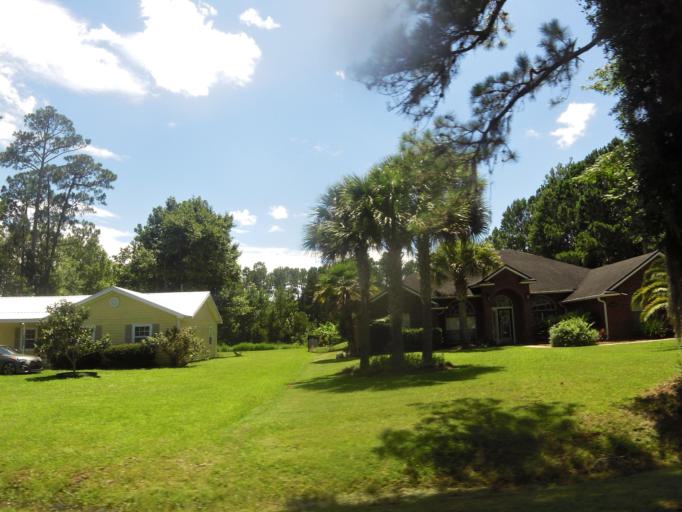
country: US
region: Georgia
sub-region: Camden County
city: St. Marys
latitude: 30.6773
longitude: -81.5320
